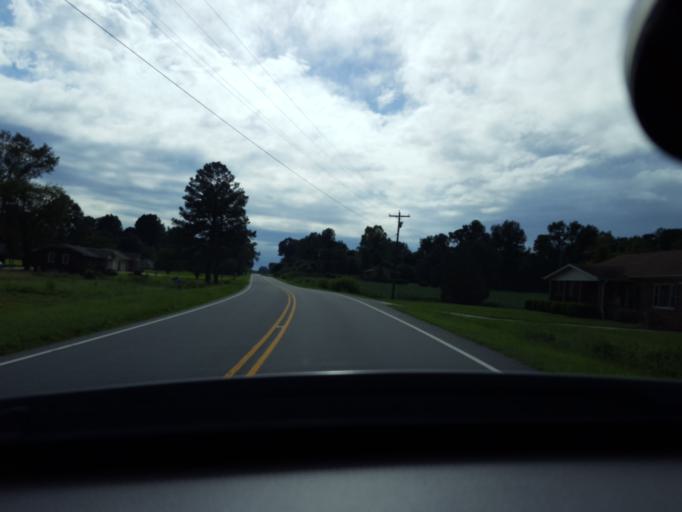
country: US
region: North Carolina
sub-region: Duplin County
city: Kenansville
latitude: 35.0123
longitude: -77.8883
